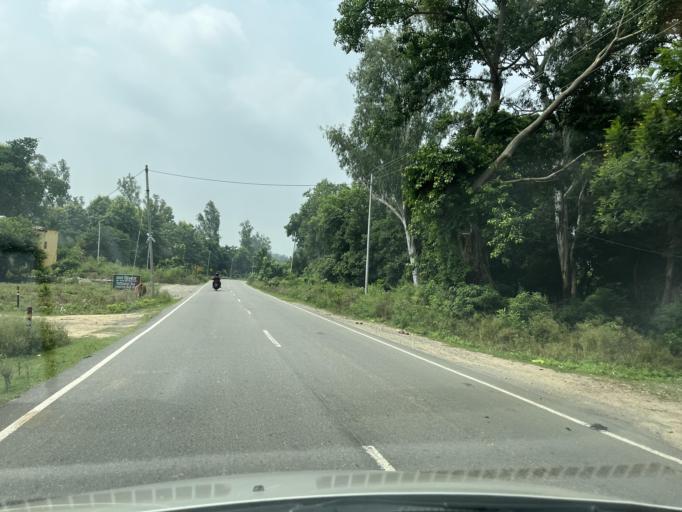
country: IN
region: Uttarakhand
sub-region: Haridwar
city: Sultanpur
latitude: 29.7505
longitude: 78.2632
